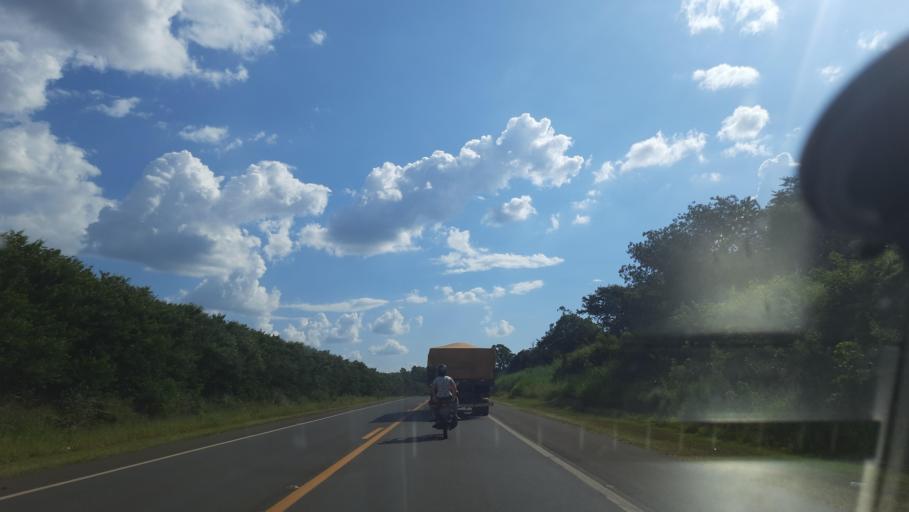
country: BR
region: Sao Paulo
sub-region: Casa Branca
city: Casa Branca
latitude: -21.7533
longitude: -46.9984
